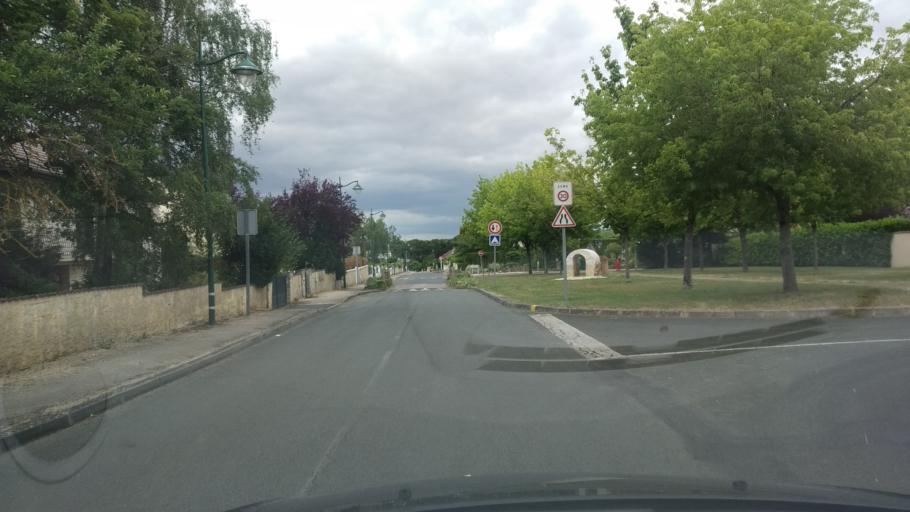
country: FR
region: Poitou-Charentes
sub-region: Departement de la Vienne
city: Vouneuil-sous-Biard
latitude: 46.5712
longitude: 0.2731
